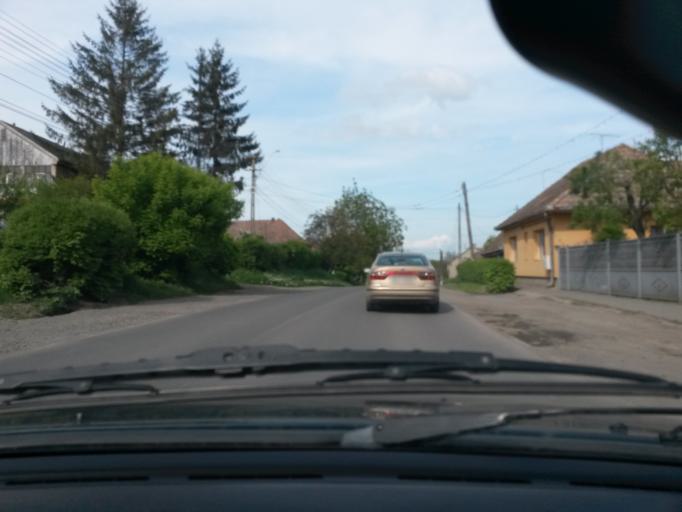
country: RO
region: Mures
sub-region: Comuna Sancraiu de Mures
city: Sancraiu de Mures
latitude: 46.5478
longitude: 24.5196
